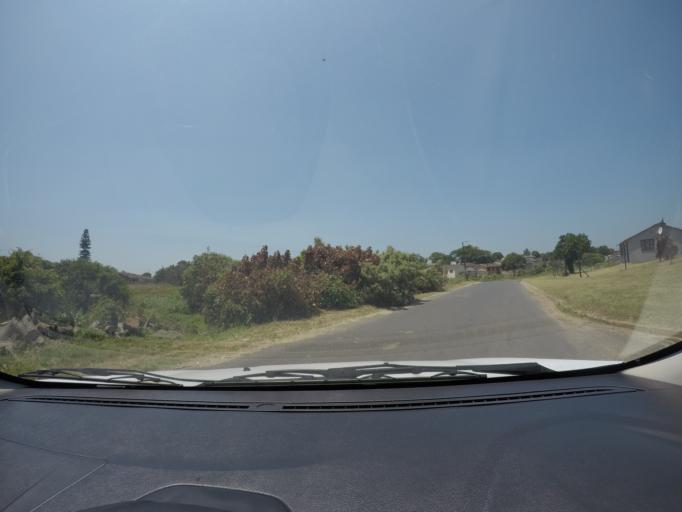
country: ZA
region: KwaZulu-Natal
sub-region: uThungulu District Municipality
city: eSikhawini
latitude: -28.8743
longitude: 31.9105
